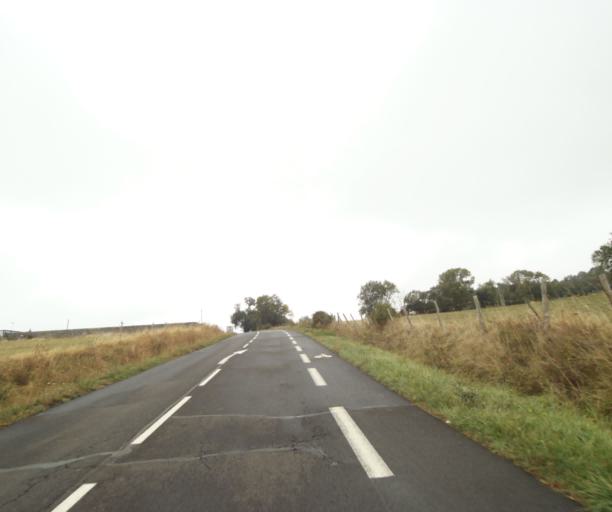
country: FR
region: Auvergne
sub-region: Departement du Puy-de-Dome
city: Romagnat
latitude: 45.7133
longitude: 3.0886
